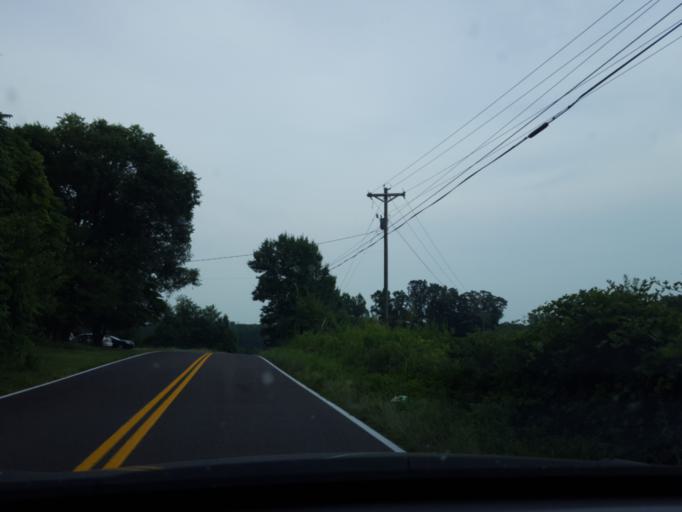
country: US
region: Virginia
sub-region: Orange County
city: Orange
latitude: 38.2641
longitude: -77.8810
